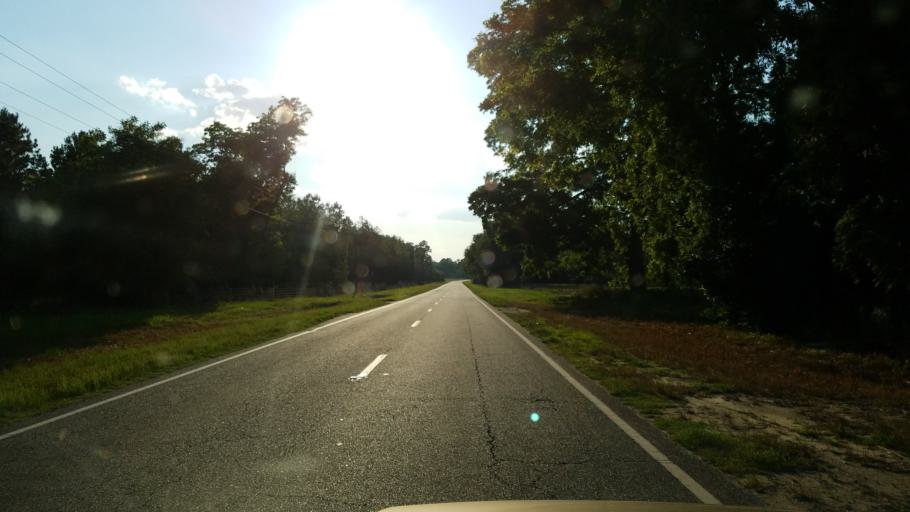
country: US
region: Georgia
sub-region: Berrien County
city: Nashville
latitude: 31.1900
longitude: -83.2033
